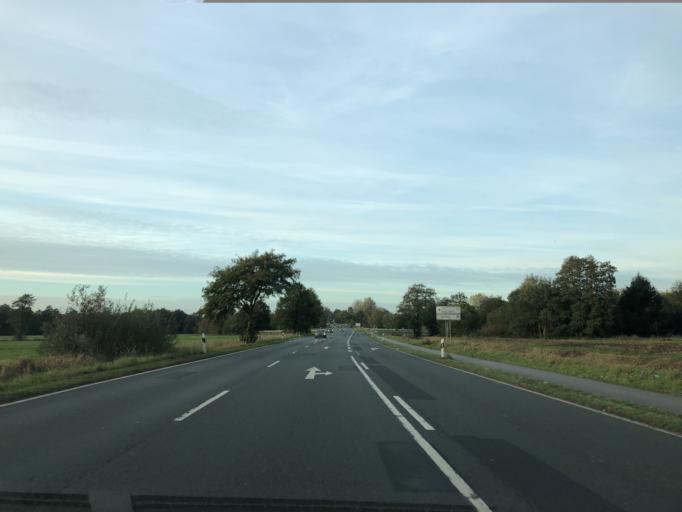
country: DE
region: Lower Saxony
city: Papenburg
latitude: 53.0777
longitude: 7.3800
